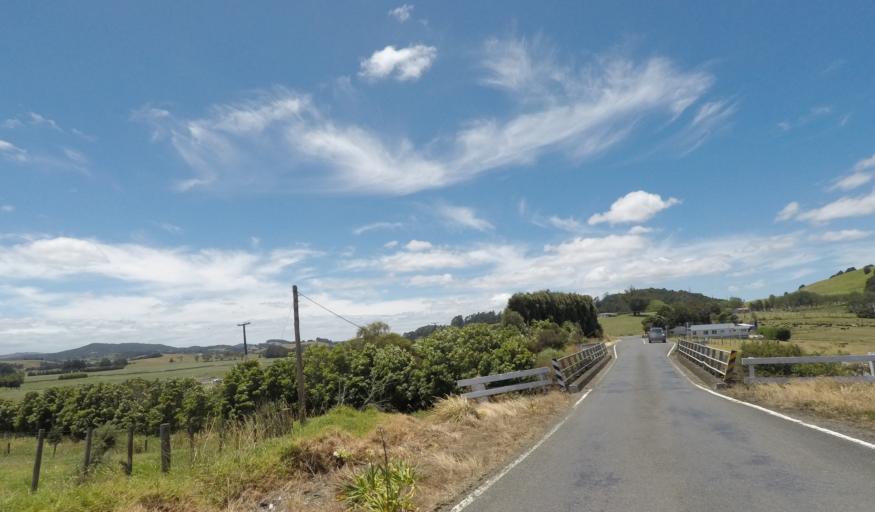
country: NZ
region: Northland
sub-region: Whangarei
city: Whangarei
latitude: -35.5601
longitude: 174.2860
